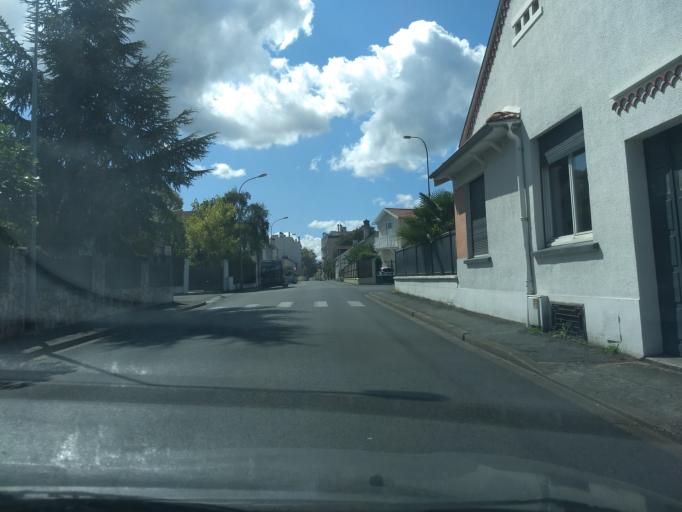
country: FR
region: Aquitaine
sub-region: Departement des Pyrenees-Atlantiques
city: Pau
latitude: 43.3074
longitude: -0.3699
